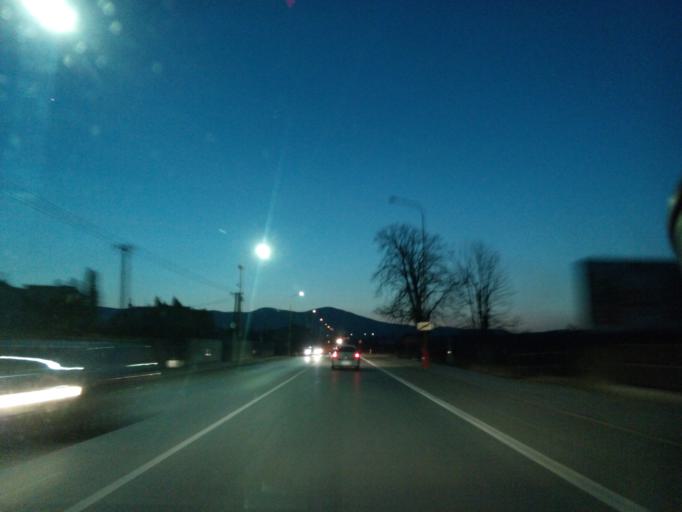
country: SK
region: Kosicky
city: Secovce
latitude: 48.7043
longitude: 21.6395
